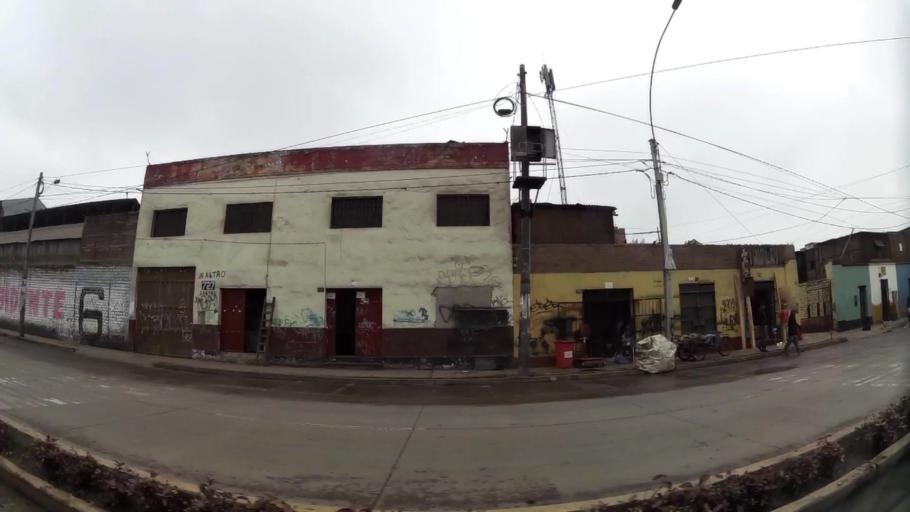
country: PE
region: Lima
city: Lima
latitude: -12.0658
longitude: -77.0211
